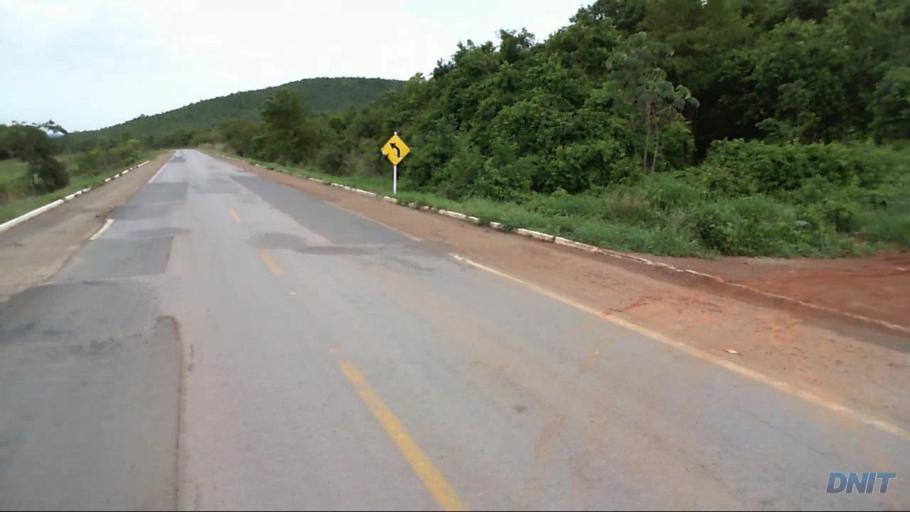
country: BR
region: Goias
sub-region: Barro Alto
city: Barro Alto
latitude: -14.9006
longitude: -48.9647
